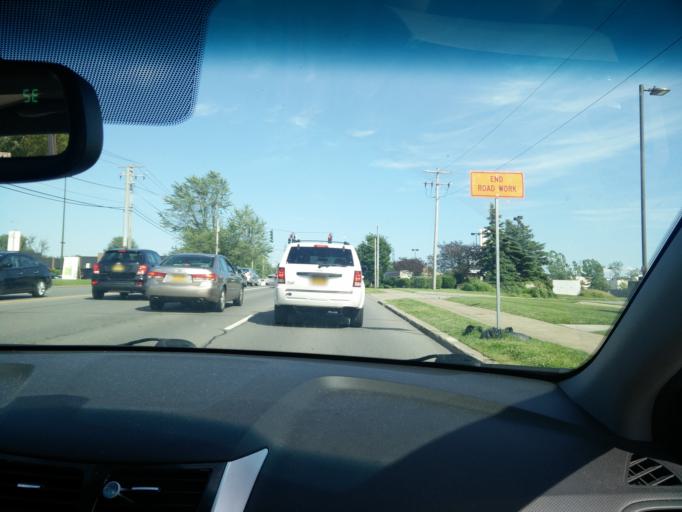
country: US
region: New York
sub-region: Erie County
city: West Seneca
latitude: 42.8352
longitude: -78.7875
